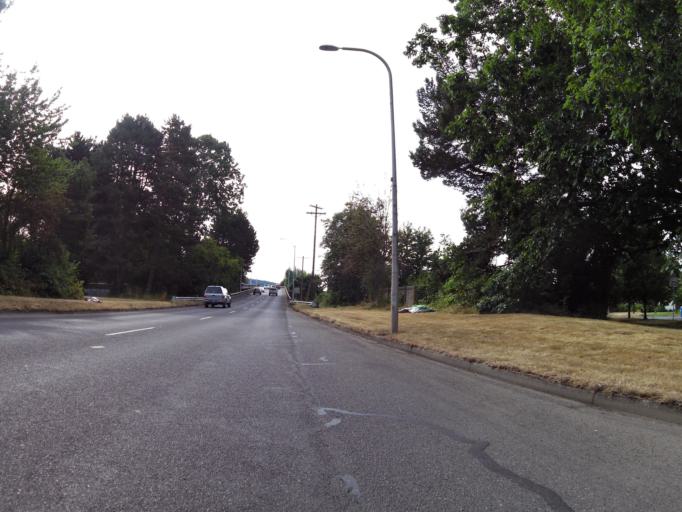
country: US
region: Washington
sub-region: Lewis County
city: Centralia
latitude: 46.7101
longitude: -122.9581
